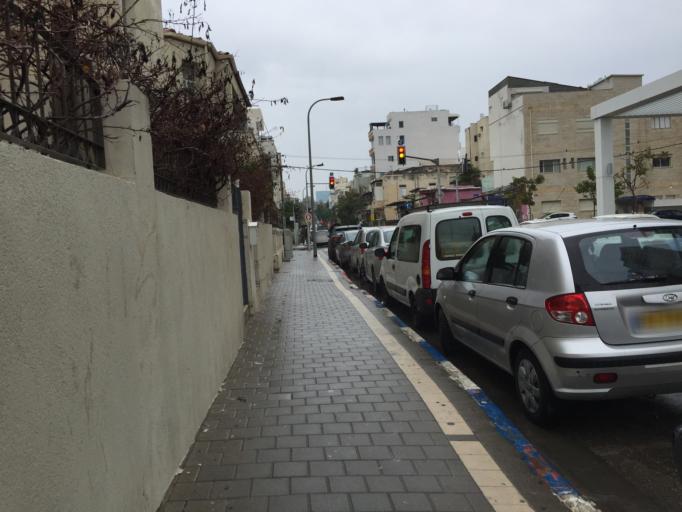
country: IL
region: Tel Aviv
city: Tel Aviv
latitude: 32.0718
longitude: 34.7649
